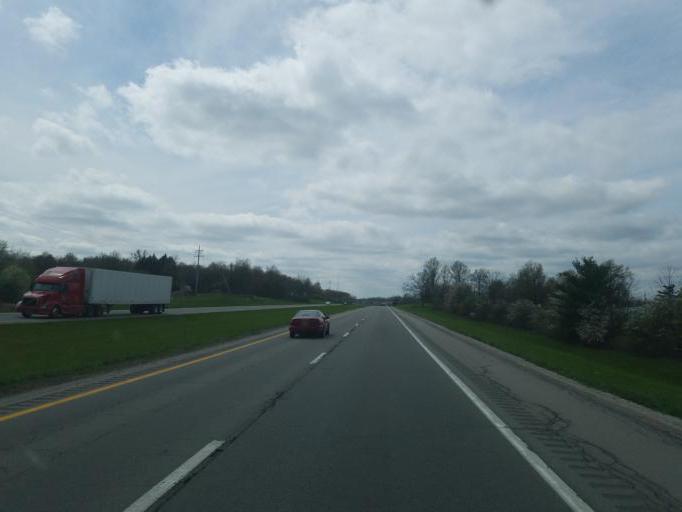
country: US
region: Ohio
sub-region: Richland County
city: Ontario
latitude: 40.7839
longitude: -82.6226
